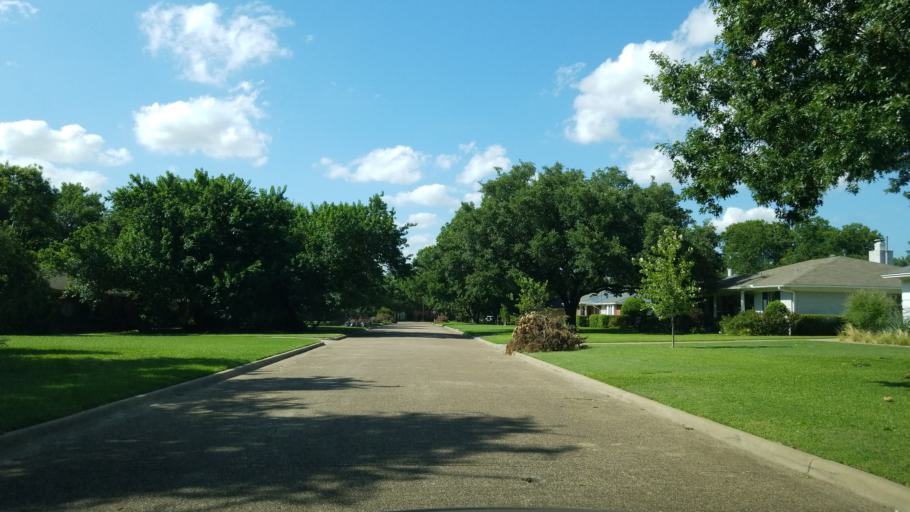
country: US
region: Texas
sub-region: Dallas County
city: University Park
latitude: 32.8860
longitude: -96.8487
